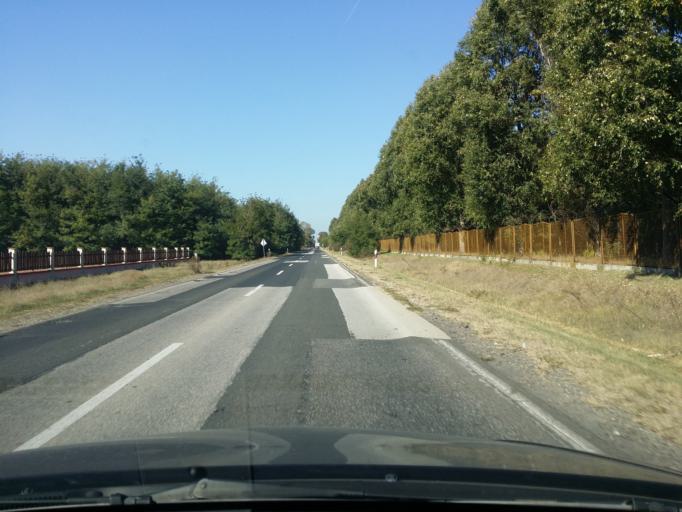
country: HU
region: Bacs-Kiskun
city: Nyarlorinc
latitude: 46.8745
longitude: 19.8507
